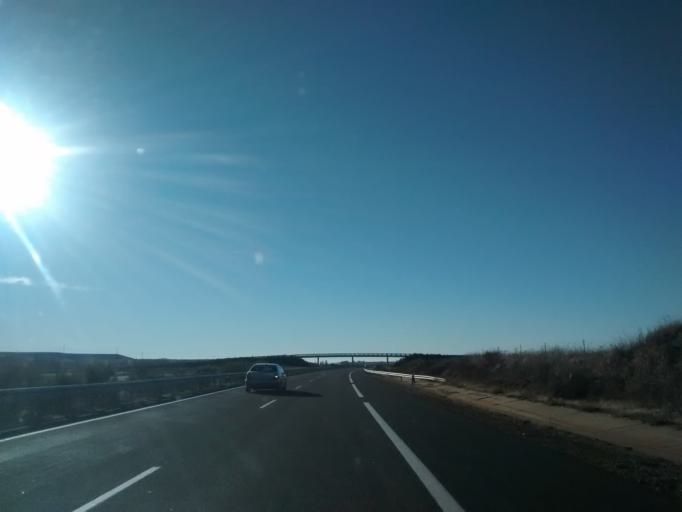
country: ES
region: Castille and Leon
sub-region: Provincia de Palencia
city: Villaprovedo
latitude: 42.5068
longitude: -4.3802
